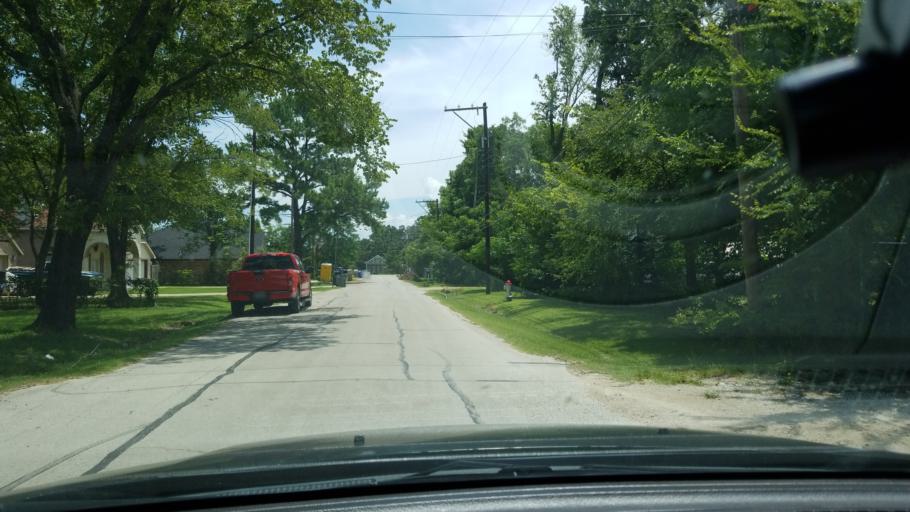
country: US
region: Texas
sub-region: Dallas County
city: Balch Springs
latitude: 32.7421
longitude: -96.6379
